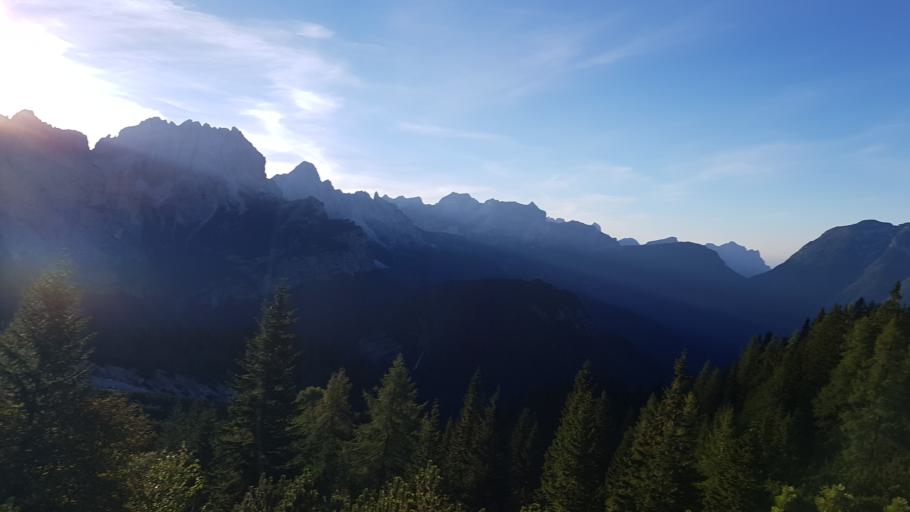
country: IT
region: Veneto
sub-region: Provincia di Belluno
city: La Valle Agordina
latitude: 46.3244
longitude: 12.0705
